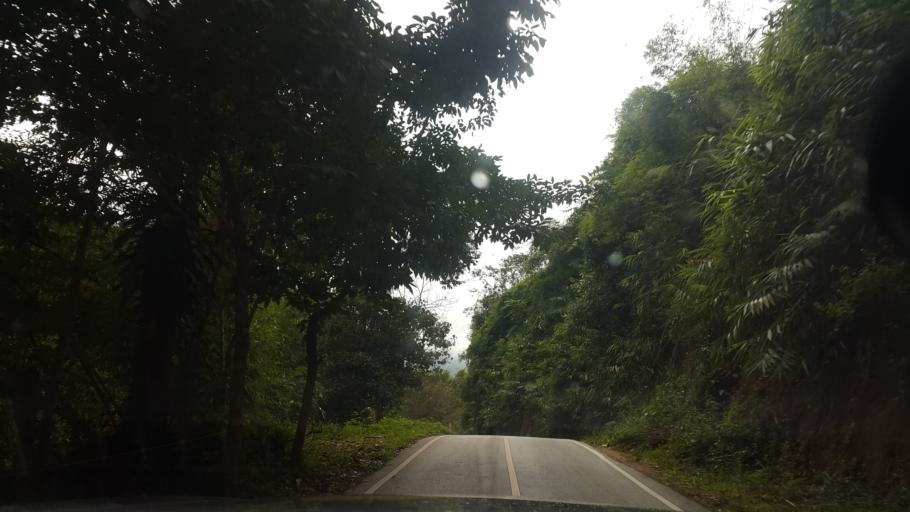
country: TH
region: Chiang Mai
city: Mae On
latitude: 18.8721
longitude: 99.3327
